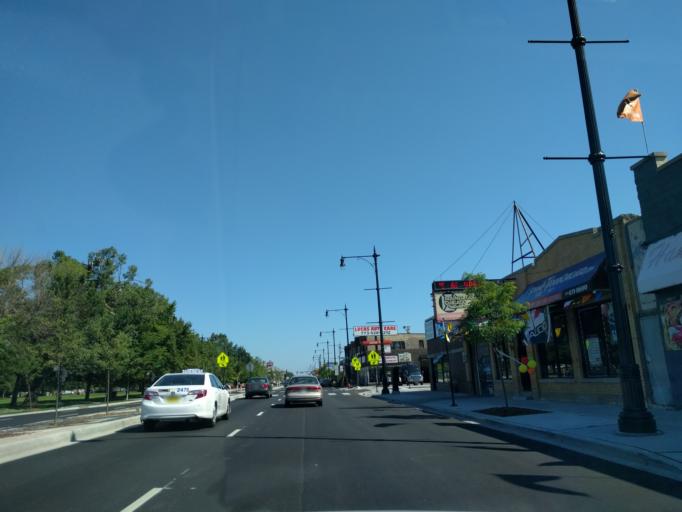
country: US
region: Illinois
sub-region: Cook County
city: Lincolnwood
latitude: 41.9445
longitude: -87.6881
